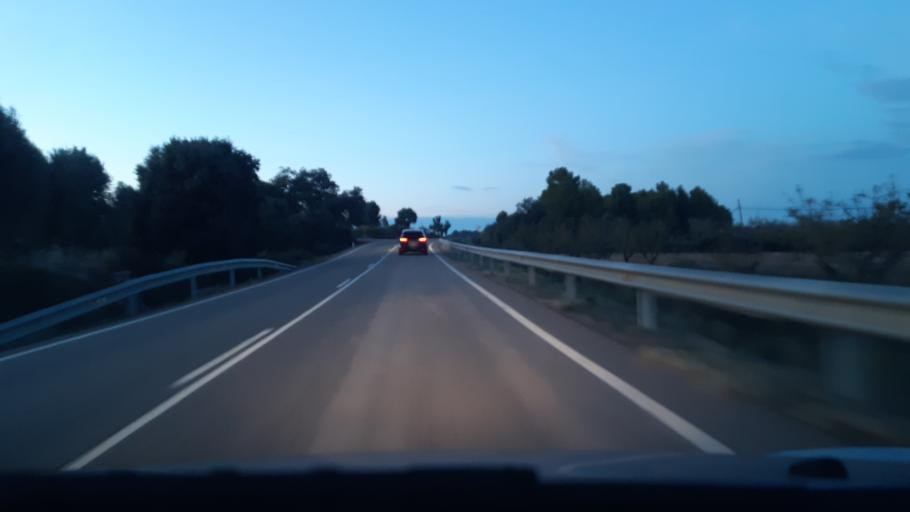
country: ES
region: Aragon
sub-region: Provincia de Teruel
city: Calaceite
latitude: 40.9854
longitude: 0.1998
